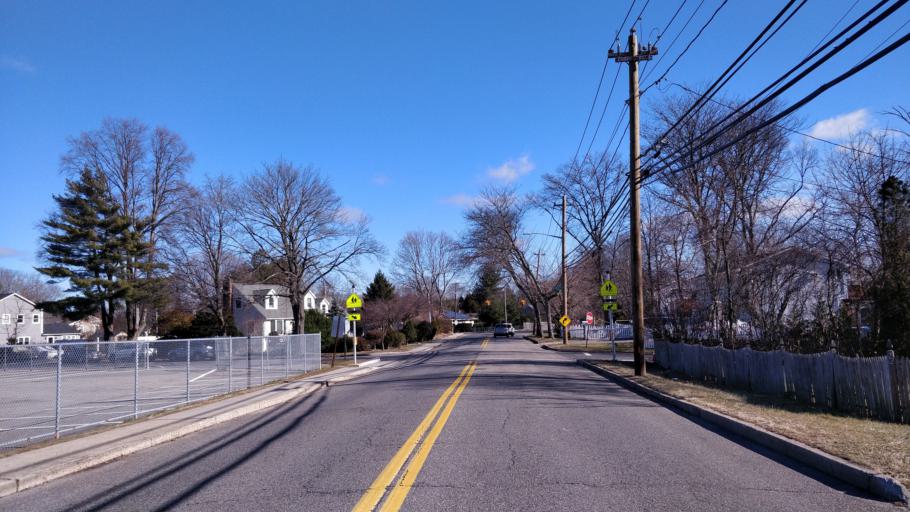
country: US
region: New York
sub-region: Suffolk County
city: Saint James
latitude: 40.8742
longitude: -73.1647
